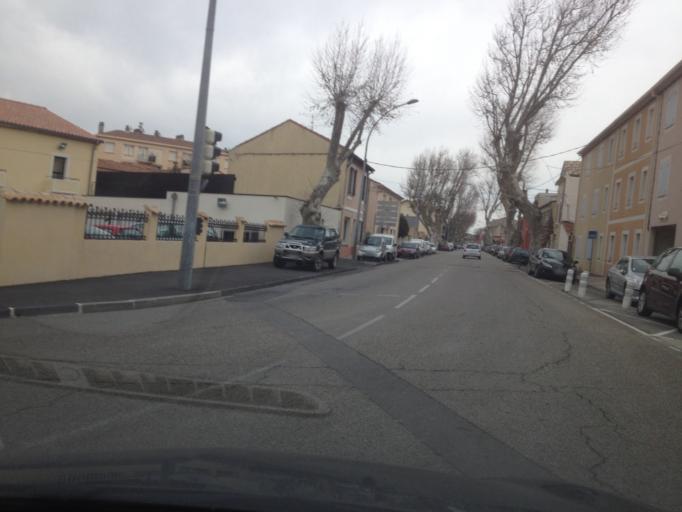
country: FR
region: Provence-Alpes-Cote d'Azur
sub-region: Departement du Vaucluse
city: Sorgues
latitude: 44.0048
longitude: 4.8703
